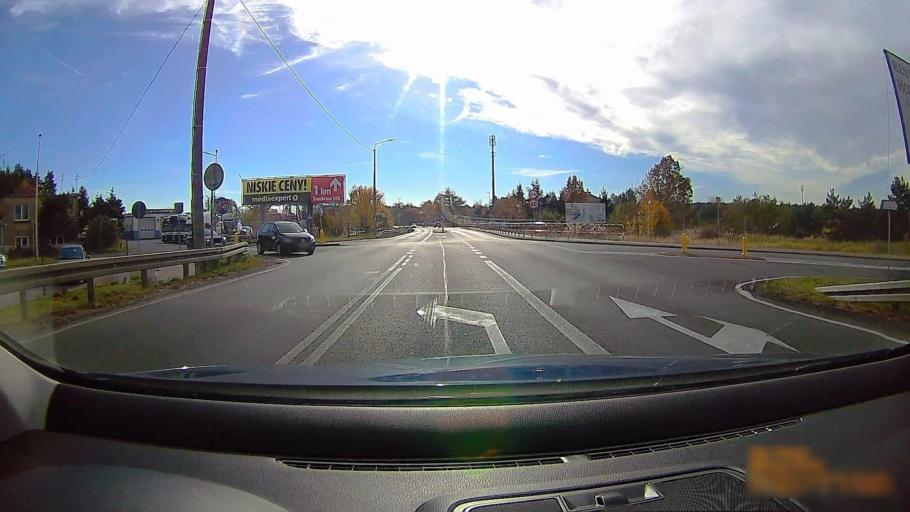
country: PL
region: Greater Poland Voivodeship
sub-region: Powiat ostrzeszowski
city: Ostrzeszow
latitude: 51.4368
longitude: 17.9151
